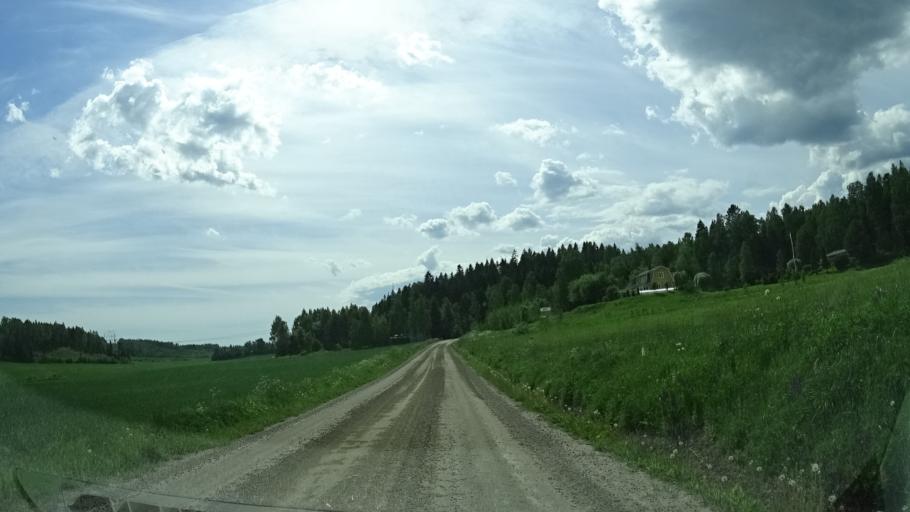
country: FI
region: Uusimaa
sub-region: Helsinki
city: Siuntio
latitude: 60.2032
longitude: 24.2600
